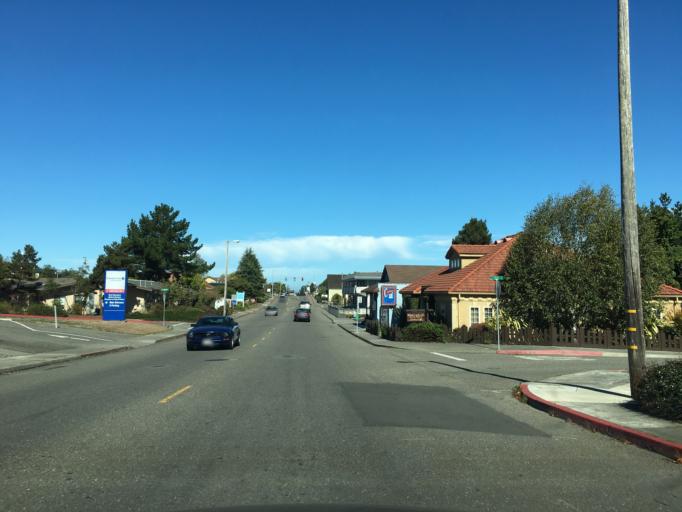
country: US
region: California
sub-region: Humboldt County
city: Myrtletown
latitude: 40.7840
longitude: -124.1396
